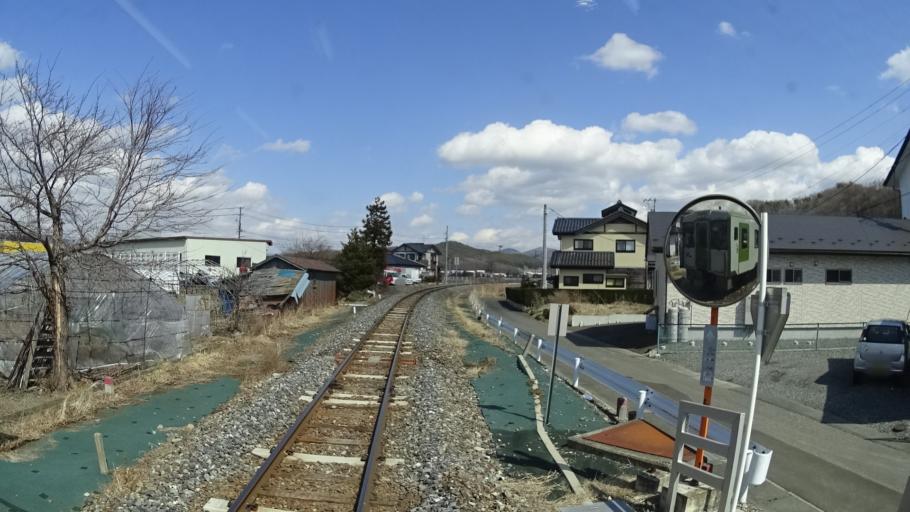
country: JP
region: Iwate
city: Tono
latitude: 39.3322
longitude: 141.5387
